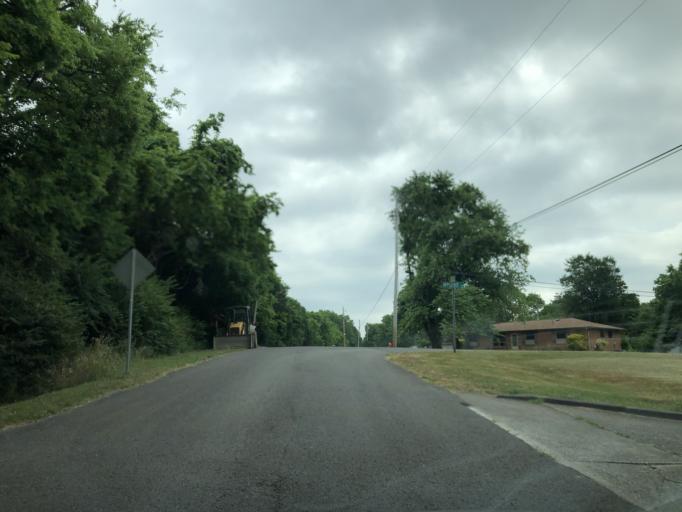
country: US
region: Tennessee
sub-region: Davidson County
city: Goodlettsville
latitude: 36.2918
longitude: -86.7296
